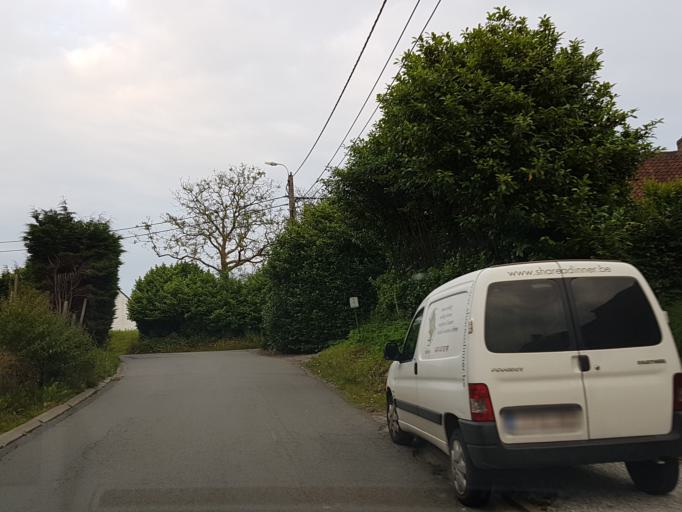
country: BE
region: Flanders
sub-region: Provincie Vlaams-Brabant
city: Asse
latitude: 50.8976
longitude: 4.1730
